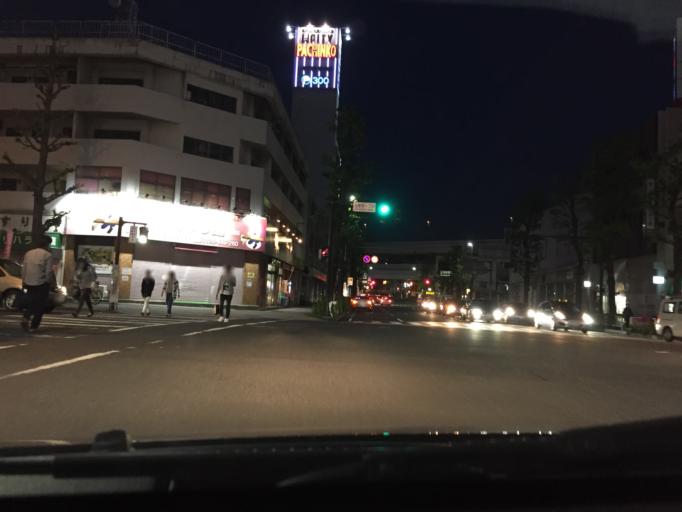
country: JP
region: Kanagawa
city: Yokohama
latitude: 35.4385
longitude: 139.6357
